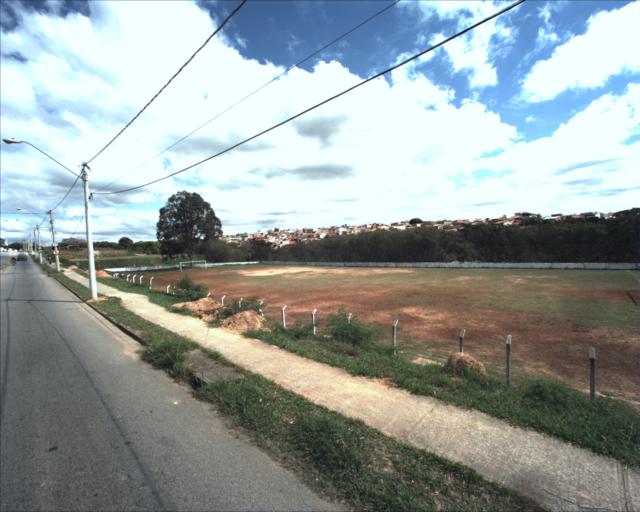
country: BR
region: Sao Paulo
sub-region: Sorocaba
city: Sorocaba
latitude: -23.4967
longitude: -47.5187
